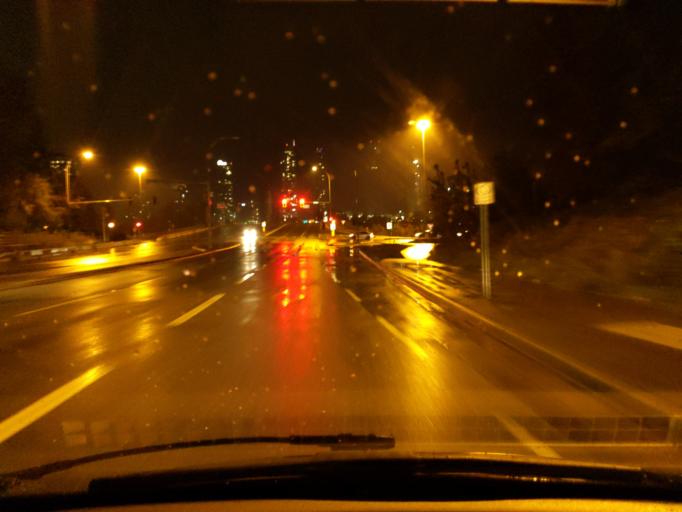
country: CA
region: British Columbia
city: Burnaby
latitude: 49.2552
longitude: -123.0041
